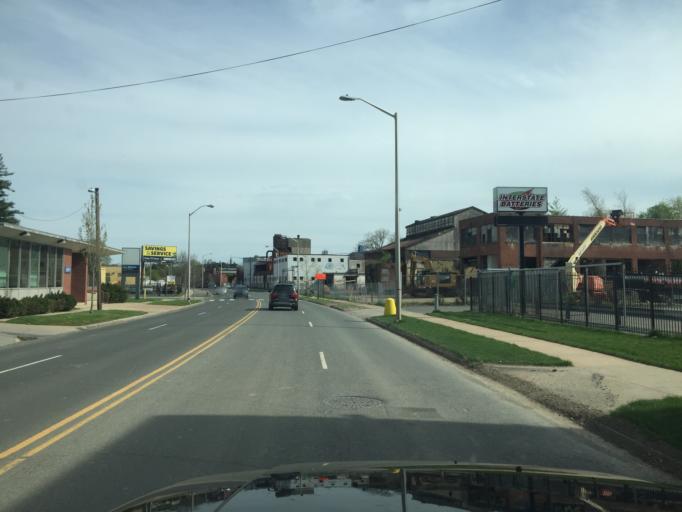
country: US
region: Connecticut
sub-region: Hartford County
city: Hartford
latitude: 41.7826
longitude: -72.7028
